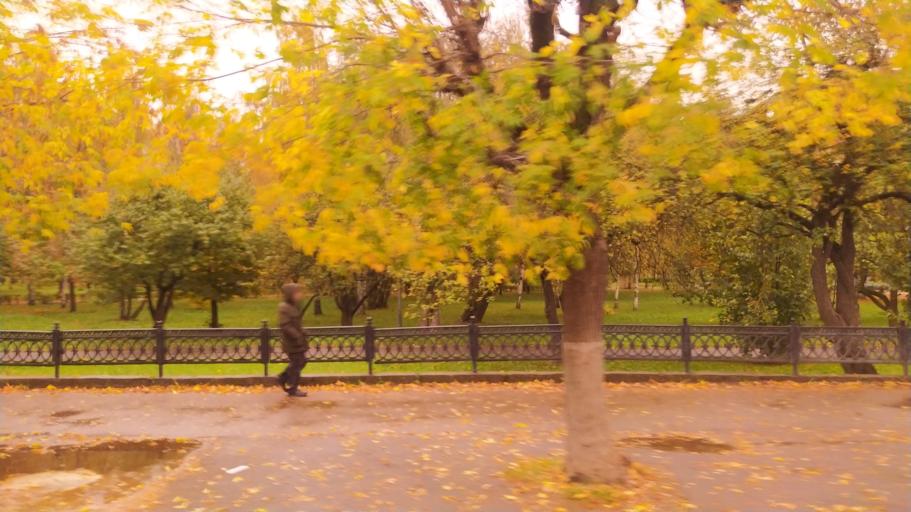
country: RU
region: Tverskaya
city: Tver
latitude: 56.8464
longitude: 35.9138
